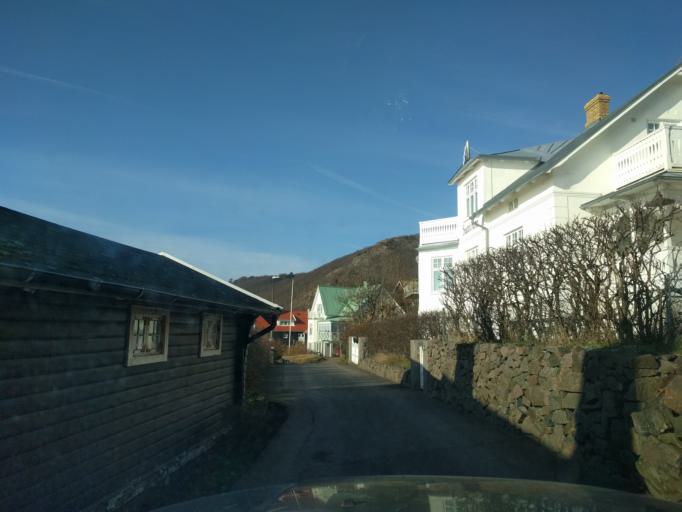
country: SE
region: Skane
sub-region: Hoganas Kommun
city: Hoganas
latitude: 56.2869
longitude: 12.4907
